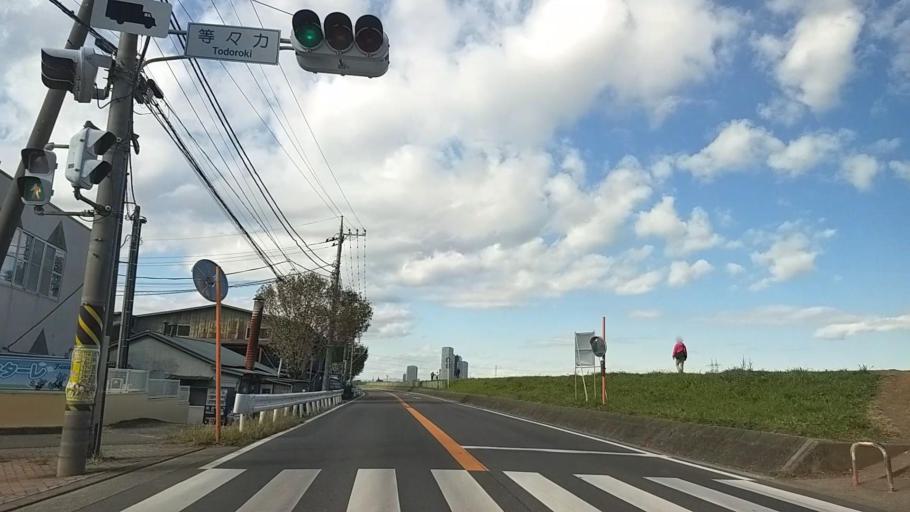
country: JP
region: Kanagawa
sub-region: Kawasaki-shi
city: Kawasaki
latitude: 35.5905
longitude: 139.6508
